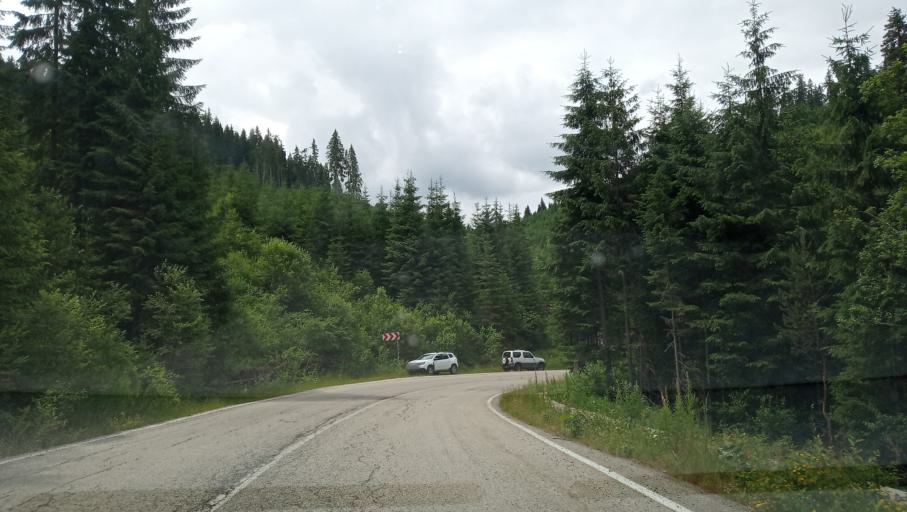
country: RO
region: Valcea
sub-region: Comuna Voineasa
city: Voineasa
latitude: 45.4231
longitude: 23.7486
